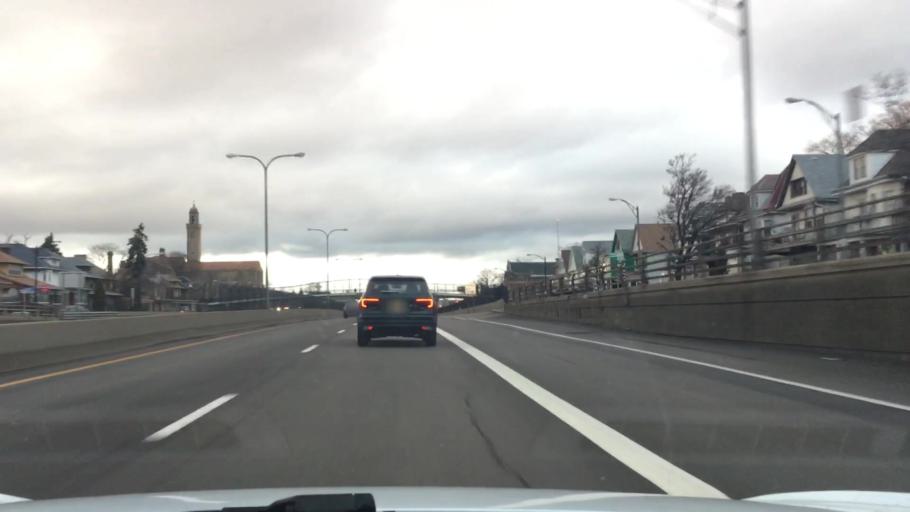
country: US
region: New York
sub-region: Erie County
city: Buffalo
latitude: 42.9164
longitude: -78.8433
